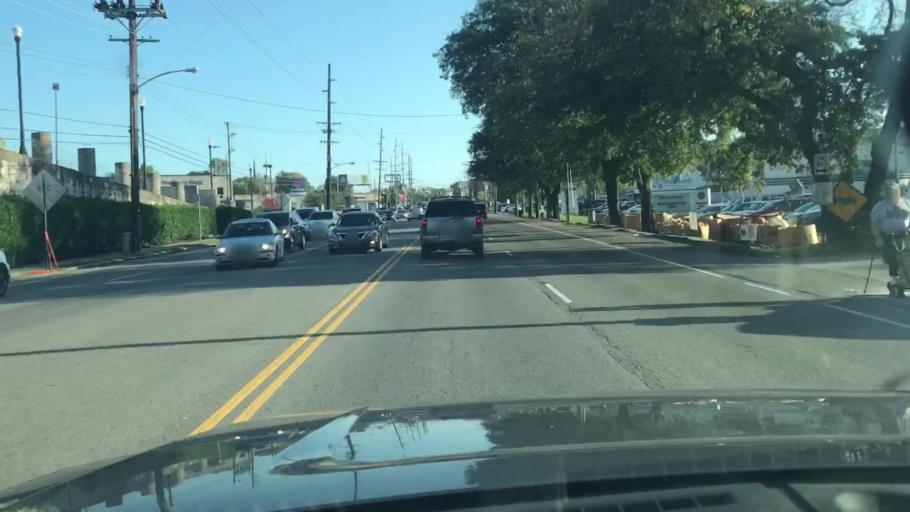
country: US
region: Tennessee
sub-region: Davidson County
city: Oak Hill
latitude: 36.1062
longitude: -86.8136
